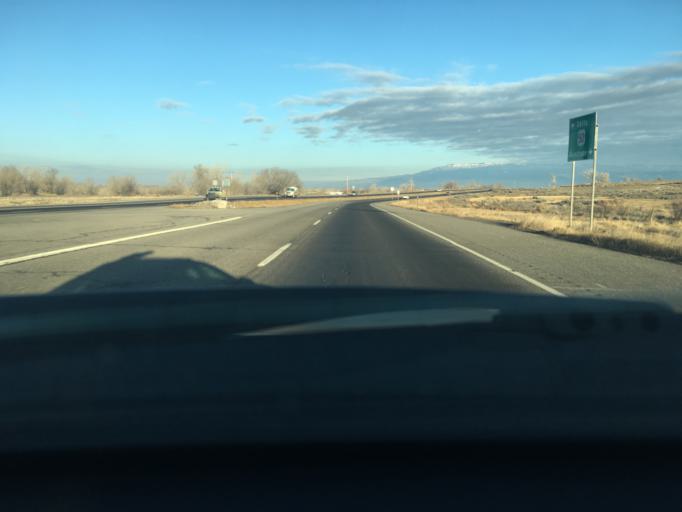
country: US
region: Colorado
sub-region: Montrose County
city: Olathe
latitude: 38.6174
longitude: -107.9826
